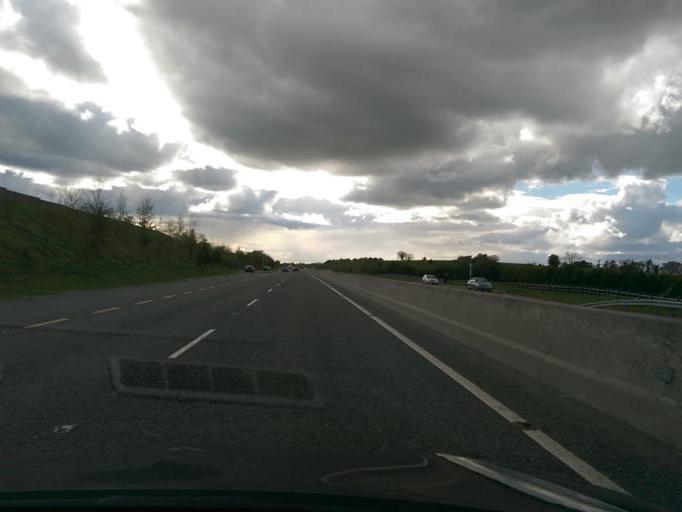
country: IE
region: Leinster
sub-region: An Iarmhi
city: Kilbeggan
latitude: 53.3596
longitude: -7.4418
